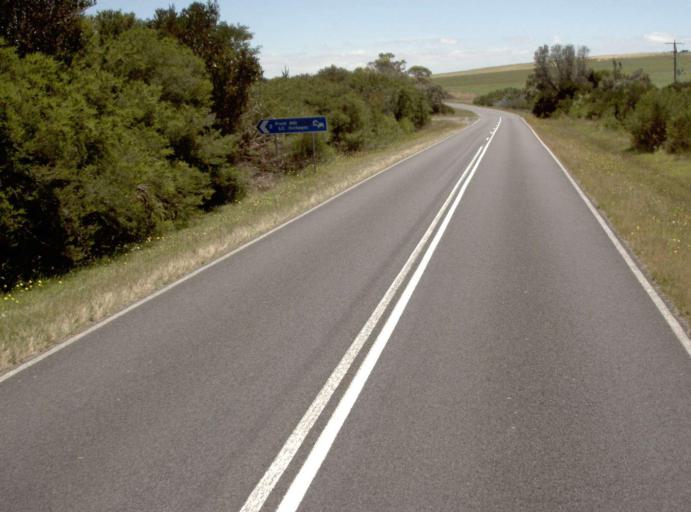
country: AU
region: Victoria
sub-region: Latrobe
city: Morwell
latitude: -38.8321
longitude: 146.2393
